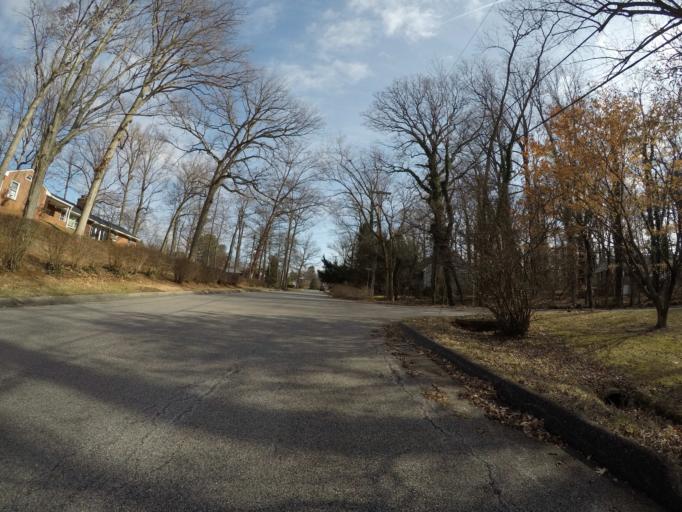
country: US
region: Maryland
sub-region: Howard County
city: Columbia
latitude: 39.2712
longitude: -76.8343
